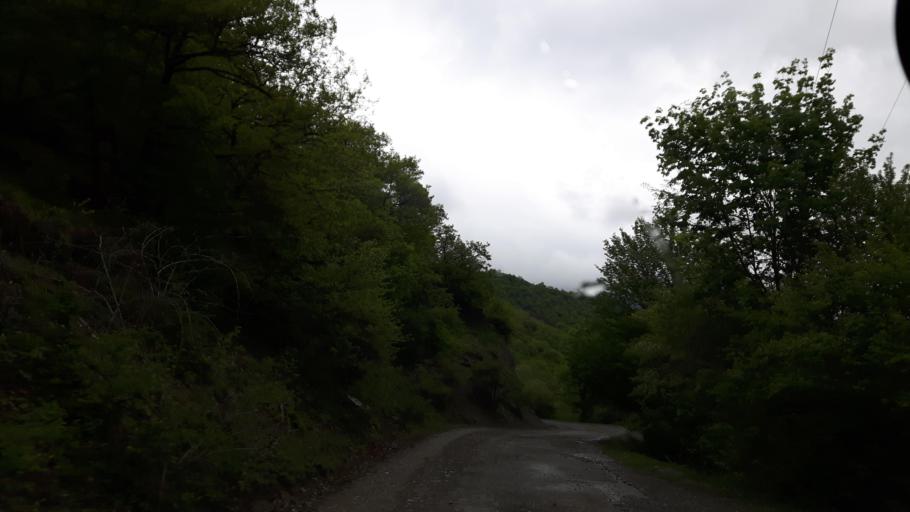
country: GE
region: Shida Kartli
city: Gori
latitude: 41.8762
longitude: 43.9896
